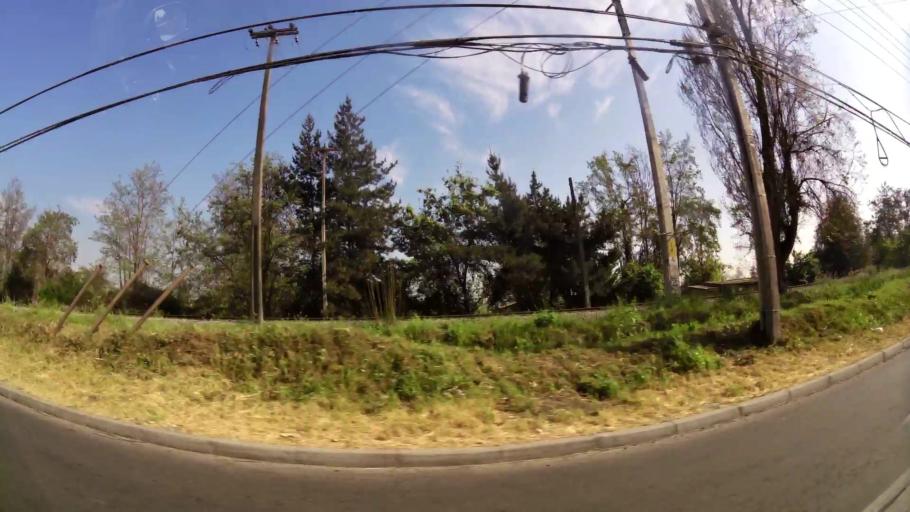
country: CL
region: Santiago Metropolitan
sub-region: Provincia de Talagante
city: Penaflor
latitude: -33.5517
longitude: -70.7925
